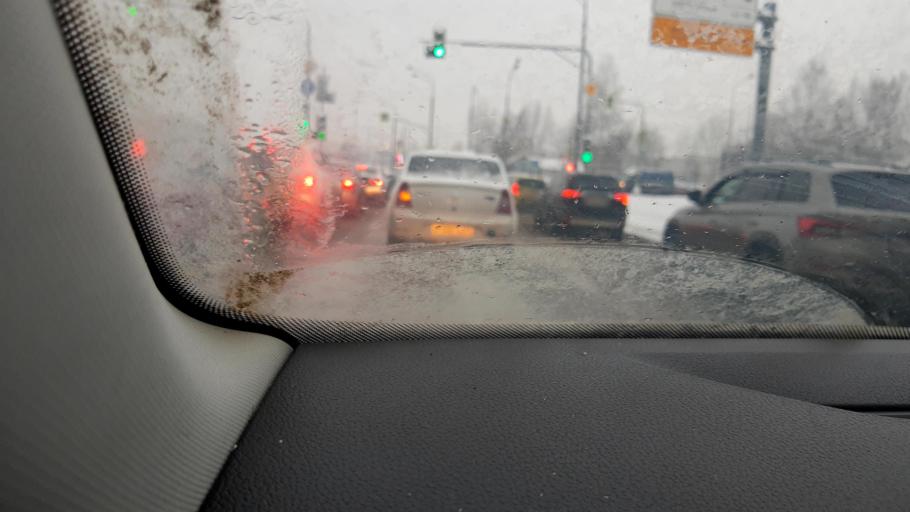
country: RU
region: Moskovskaya
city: Biryulevo Zapadnoye
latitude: 55.6038
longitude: 37.6244
